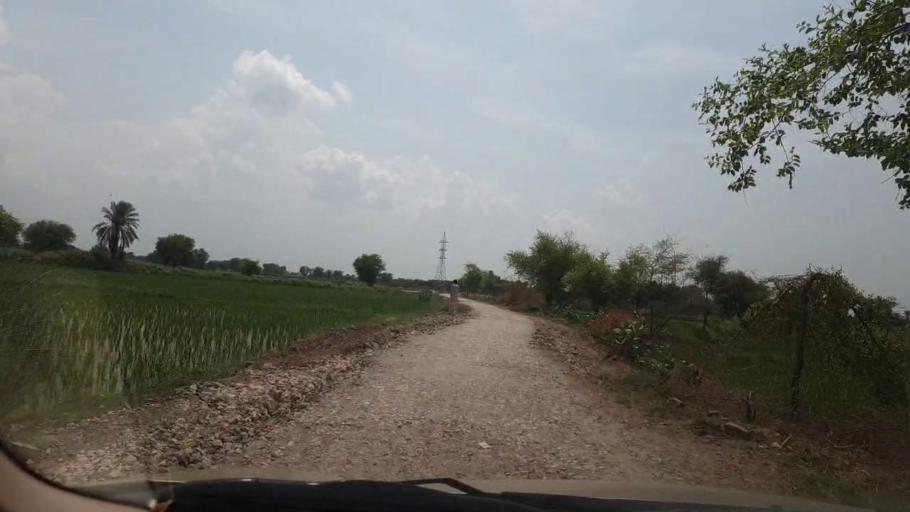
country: PK
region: Sindh
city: Larkana
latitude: 27.5743
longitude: 68.1126
